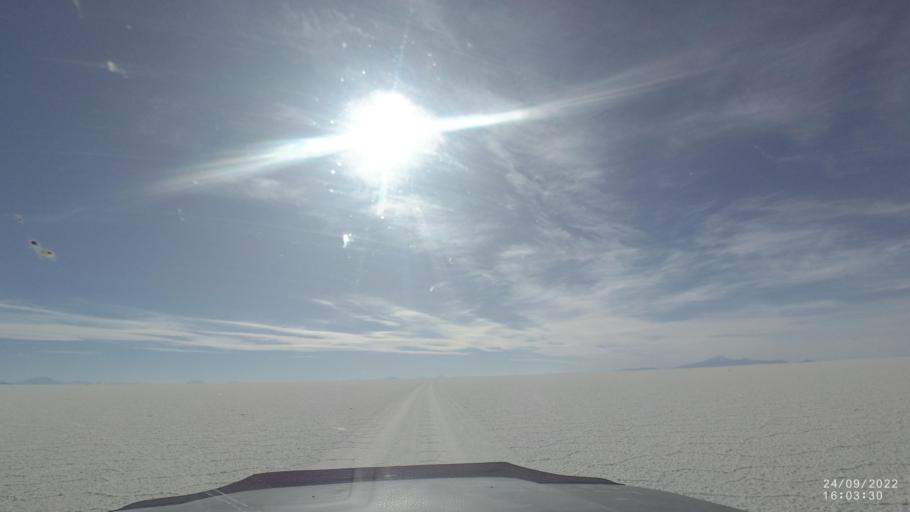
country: BO
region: Potosi
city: Colchani
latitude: -20.3129
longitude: -67.2828
